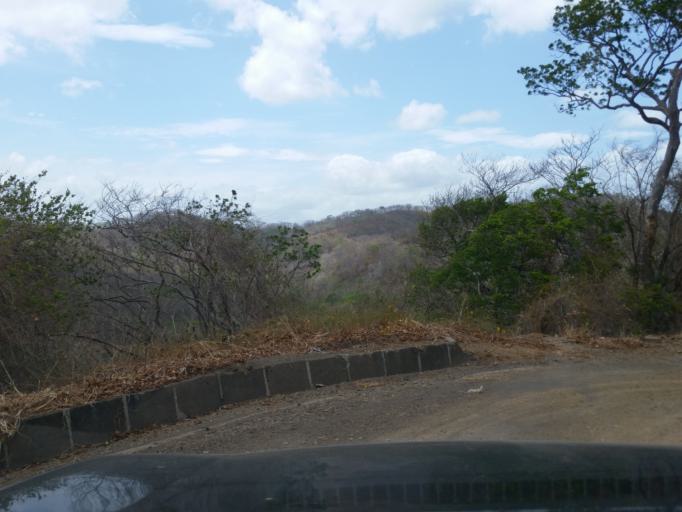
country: NI
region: Rivas
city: Tola
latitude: 11.4332
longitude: -86.0787
